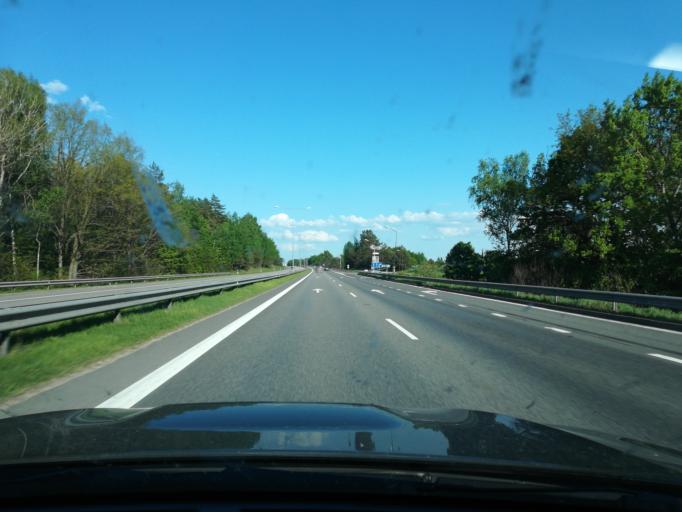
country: LT
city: Ziezmariai
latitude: 54.8037
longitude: 24.5008
